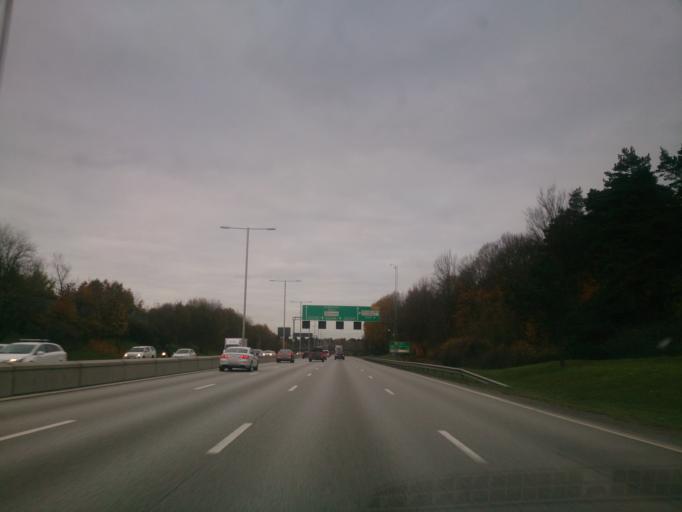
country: SE
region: Stockholm
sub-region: Solna Kommun
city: Solna
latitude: 59.3833
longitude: 18.0073
